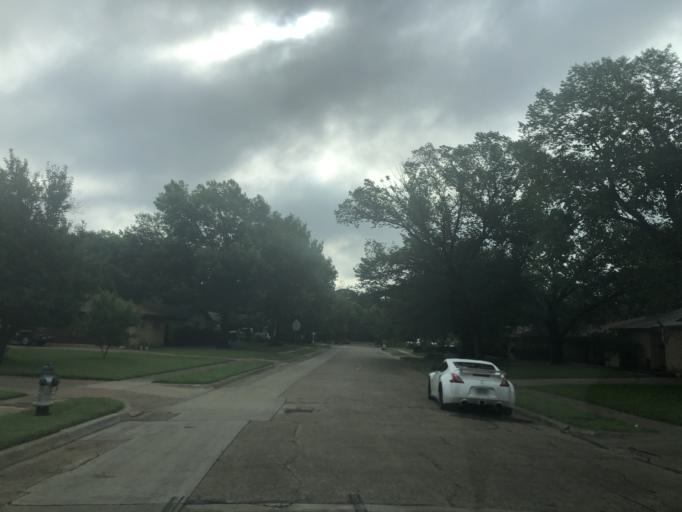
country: US
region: Texas
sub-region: Dallas County
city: Irving
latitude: 32.8058
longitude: -96.9766
